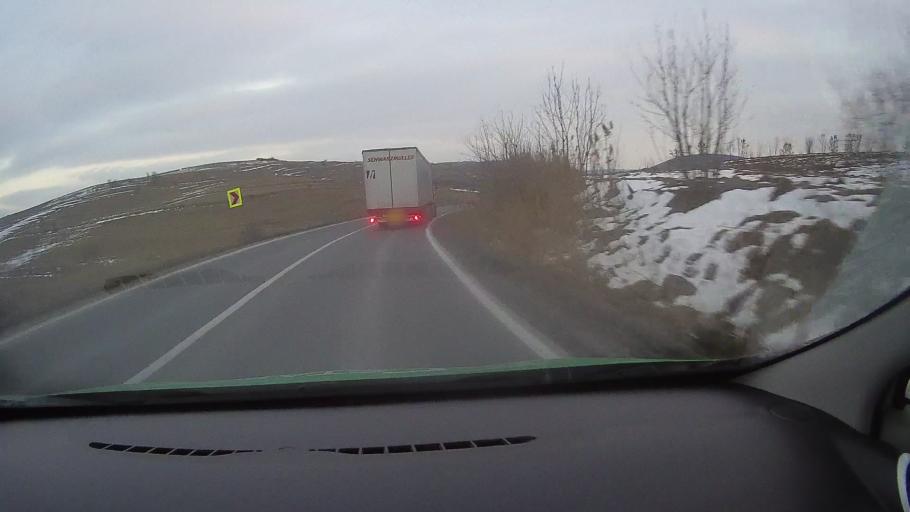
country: RO
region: Harghita
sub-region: Comuna Lupeni
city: Lupeni
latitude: 46.3504
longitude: 25.2625
